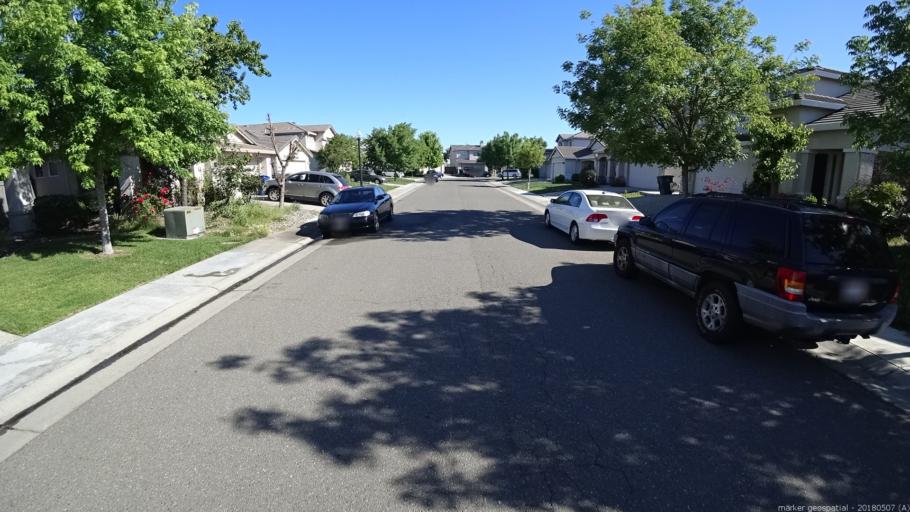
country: US
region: California
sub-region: Sacramento County
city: Rio Linda
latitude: 38.6733
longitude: -121.4948
